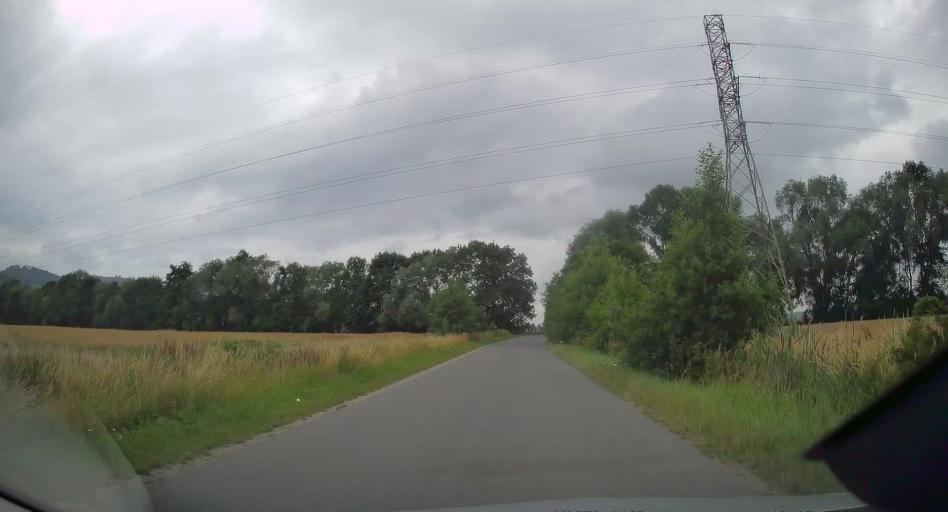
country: PL
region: Lower Silesian Voivodeship
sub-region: Powiat zabkowicki
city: Budzow
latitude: 50.5675
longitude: 16.6844
